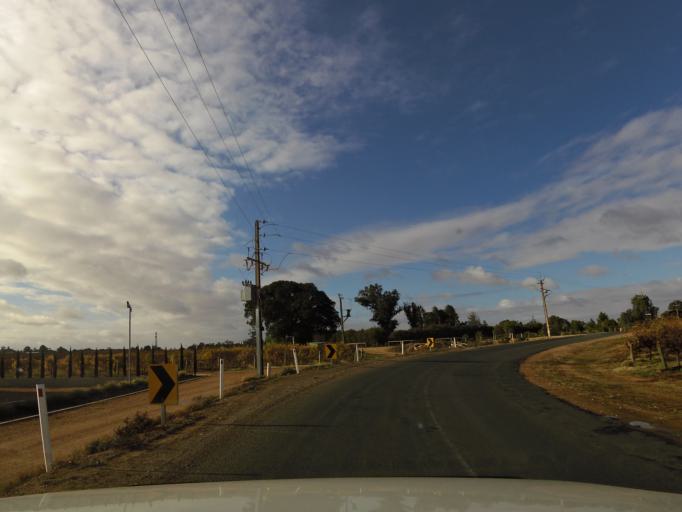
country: AU
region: South Australia
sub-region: Berri and Barmera
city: Berri
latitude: -34.2775
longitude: 140.5790
